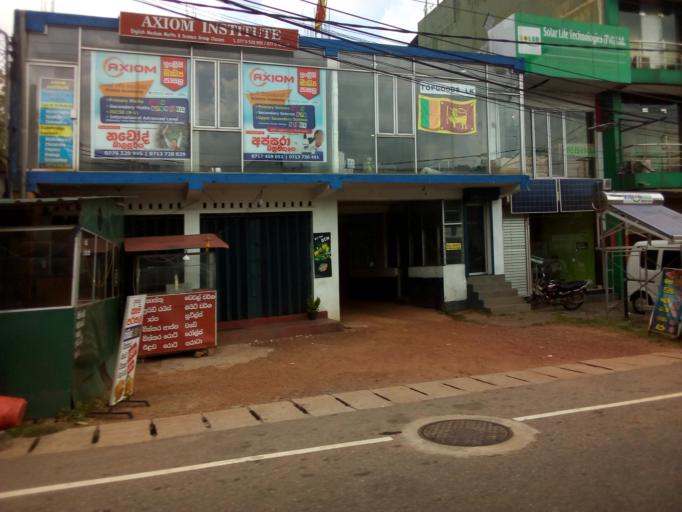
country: LK
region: Western
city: Maharagama
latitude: 6.8435
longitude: 79.9581
